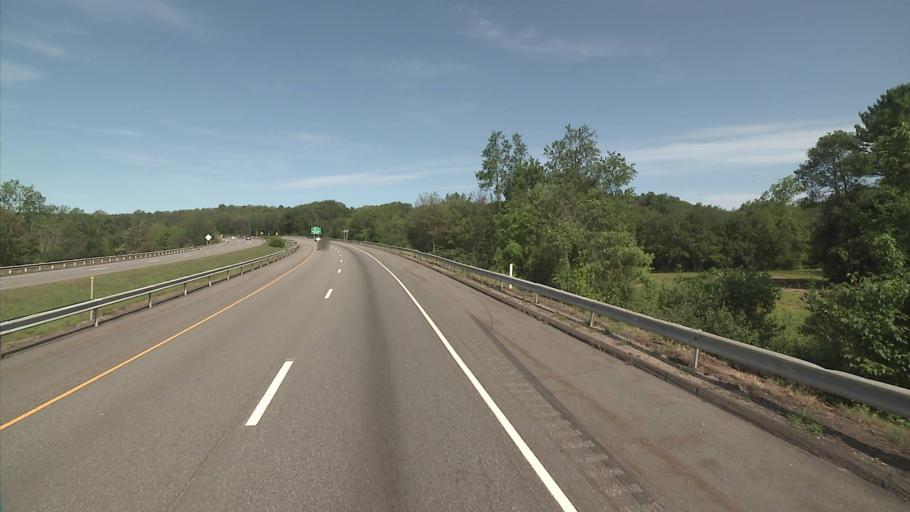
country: US
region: Connecticut
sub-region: New London County
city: Colchester
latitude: 41.5905
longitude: -72.3909
